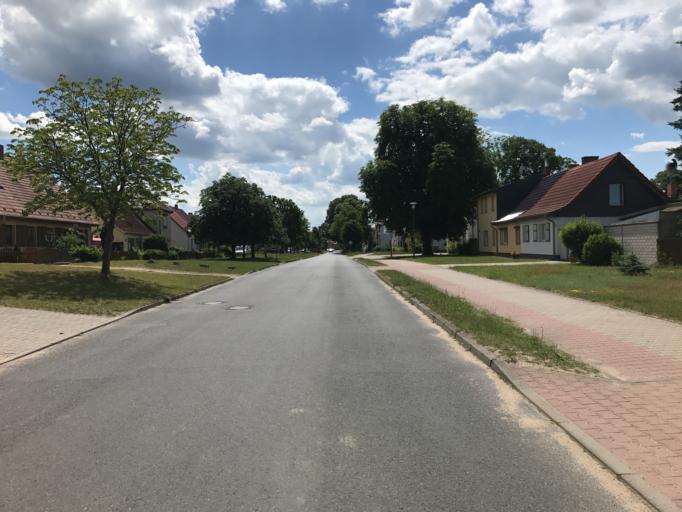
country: DE
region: Brandenburg
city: Melchow
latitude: 52.8420
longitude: 13.6816
